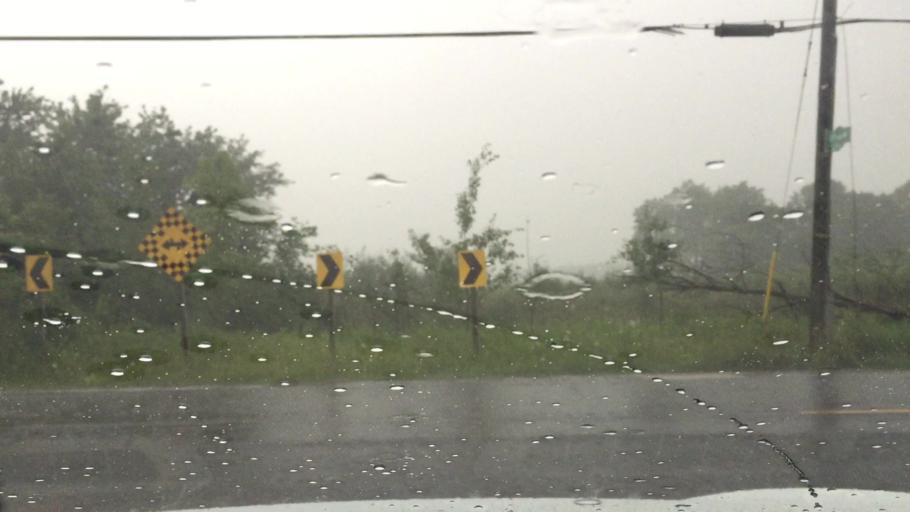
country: CA
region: Ontario
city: Markham
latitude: 43.8660
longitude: -79.2060
